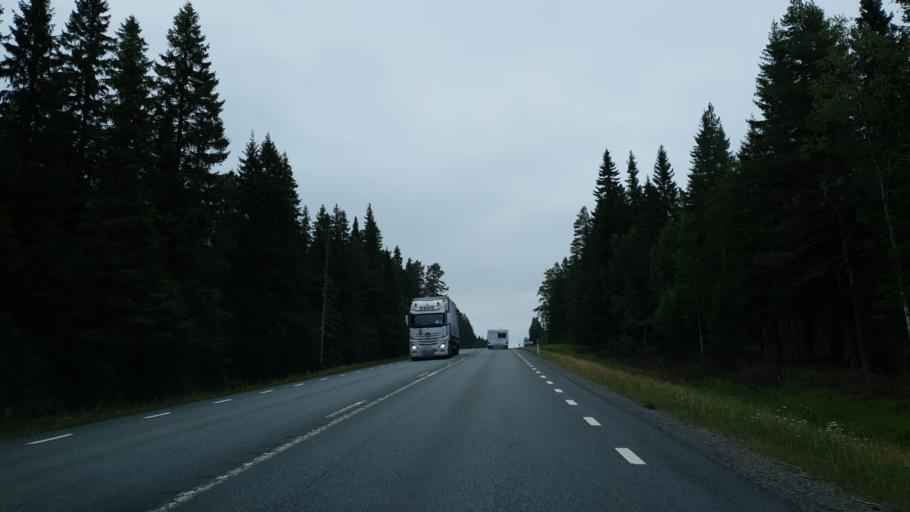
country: SE
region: Vaesterbotten
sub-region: Skelleftea Kommun
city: Burea
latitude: 64.3574
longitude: 21.2955
